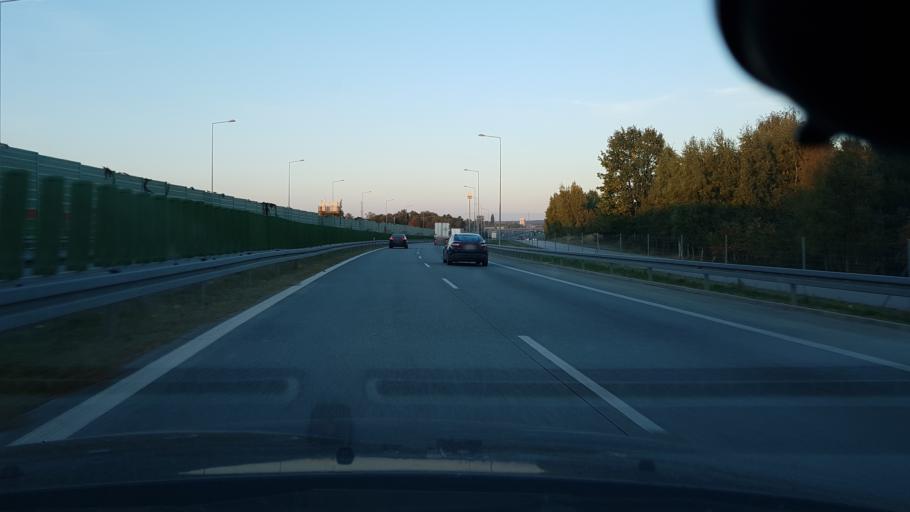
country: PL
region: Lodz Voivodeship
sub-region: Powiat rawski
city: Rawa Mazowiecka
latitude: 51.7447
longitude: 20.2374
